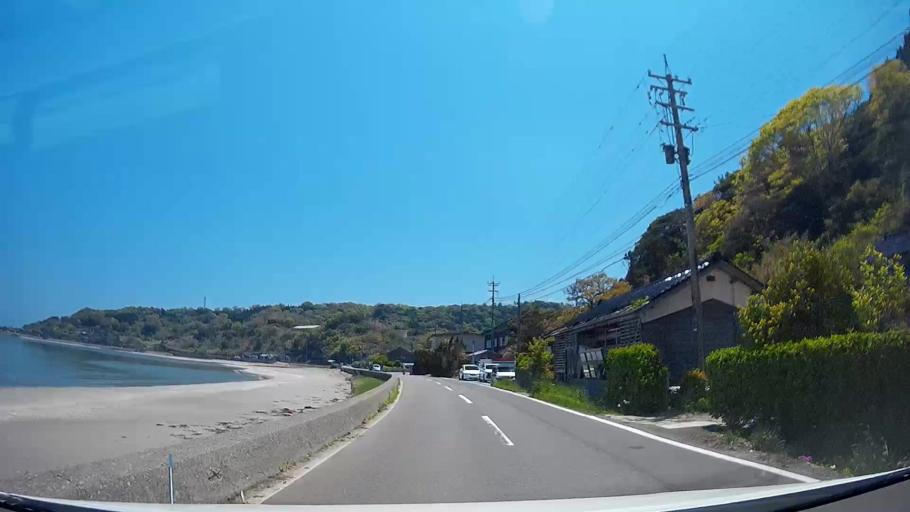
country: JP
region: Ishikawa
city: Nanao
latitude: 37.5279
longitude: 137.2791
